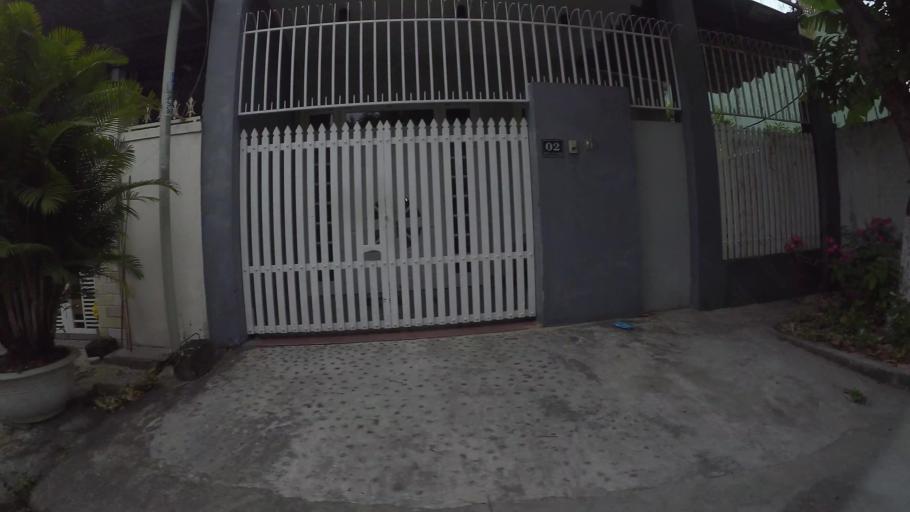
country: VN
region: Da Nang
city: Cam Le
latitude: 16.0427
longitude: 108.2075
